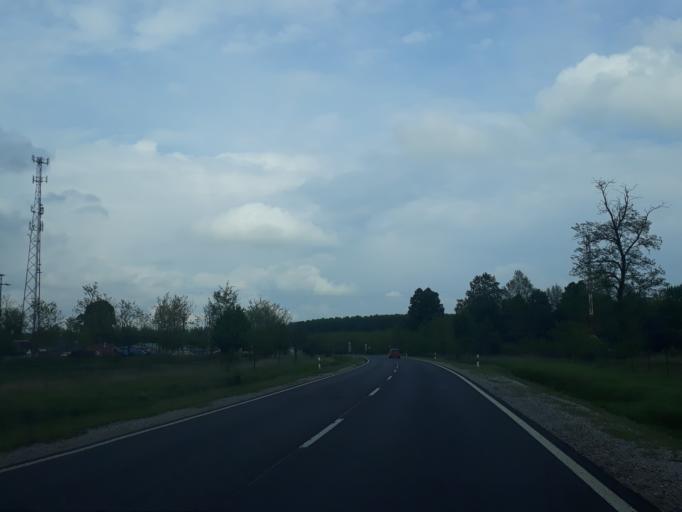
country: HU
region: Szabolcs-Szatmar-Bereg
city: Nyirbogdany
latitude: 48.0446
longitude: 21.8809
